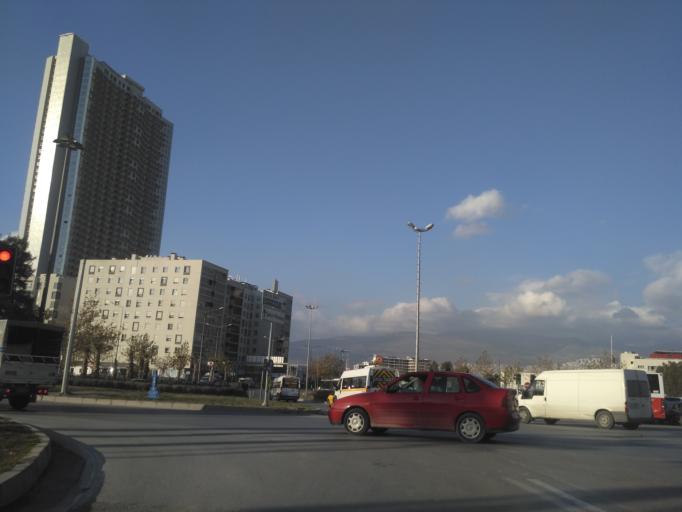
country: TR
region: Izmir
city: Buca
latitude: 38.4282
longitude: 27.2131
